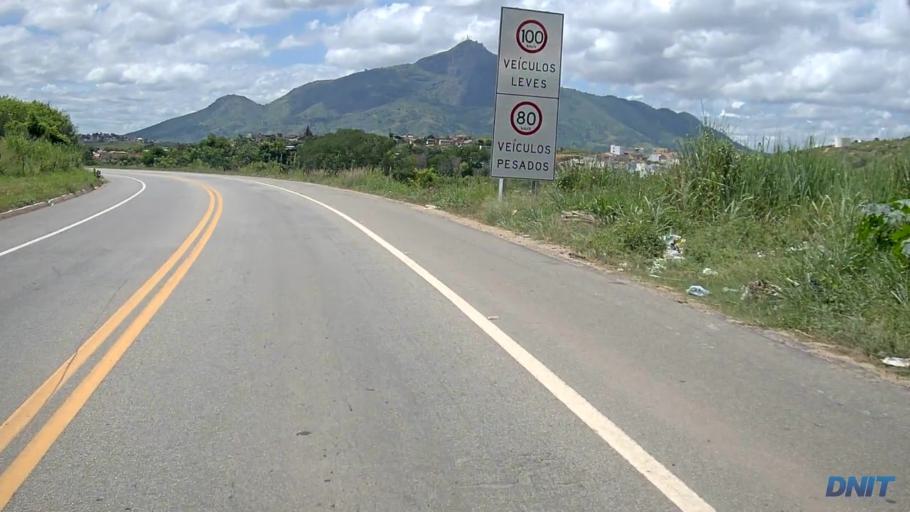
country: BR
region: Minas Gerais
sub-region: Governador Valadares
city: Governador Valadares
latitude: -18.8865
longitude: -42.0003
